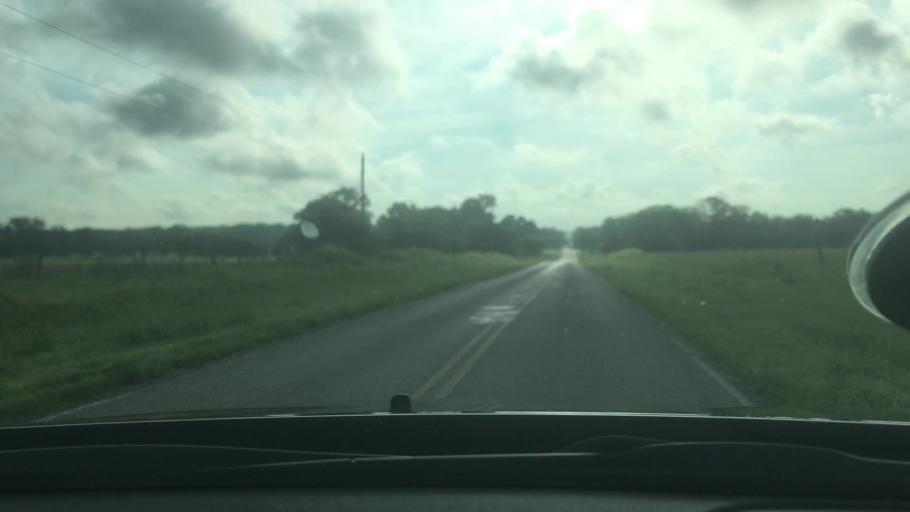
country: US
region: Oklahoma
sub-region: Pontotoc County
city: Ada
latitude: 34.6946
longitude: -96.5339
